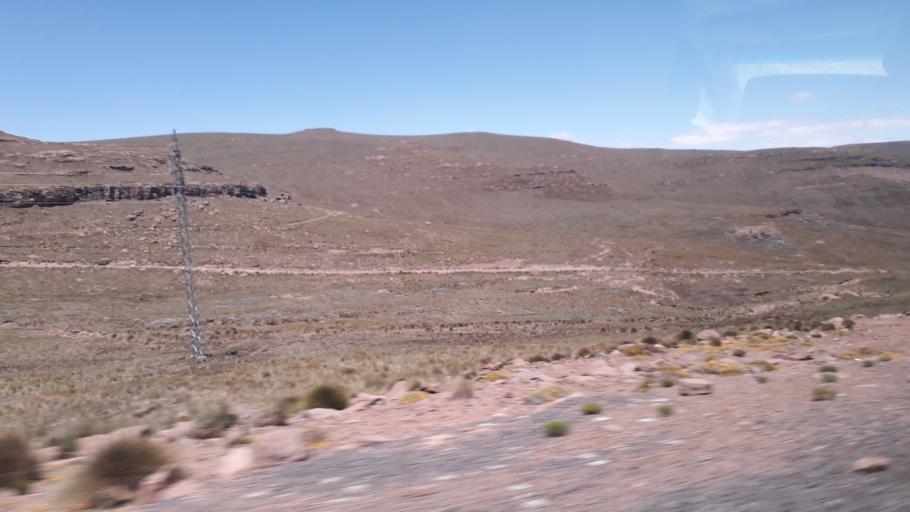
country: ZA
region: Orange Free State
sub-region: Thabo Mofutsanyana District Municipality
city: Phuthaditjhaba
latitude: -28.8089
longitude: 28.7089
